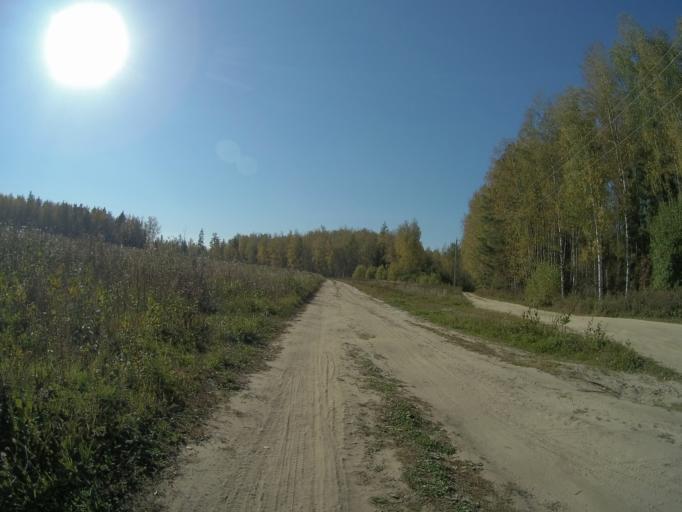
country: RU
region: Vladimir
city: Raduzhnyy
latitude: 55.9866
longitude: 40.2129
